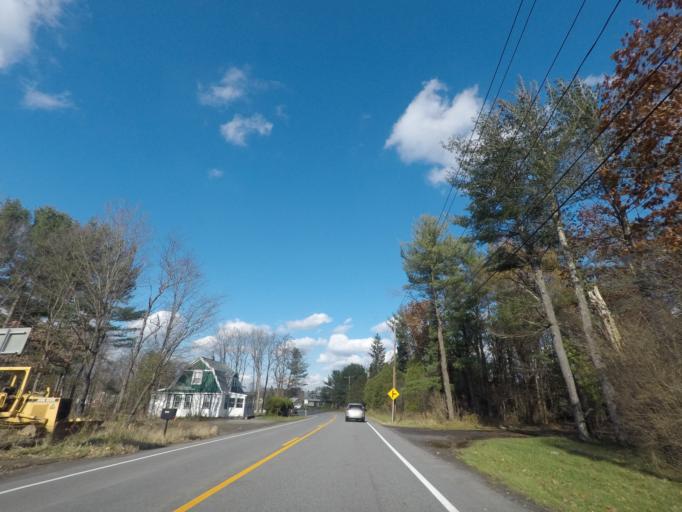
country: US
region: New York
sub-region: Schenectady County
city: East Glenville
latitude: 42.9060
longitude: -73.8742
